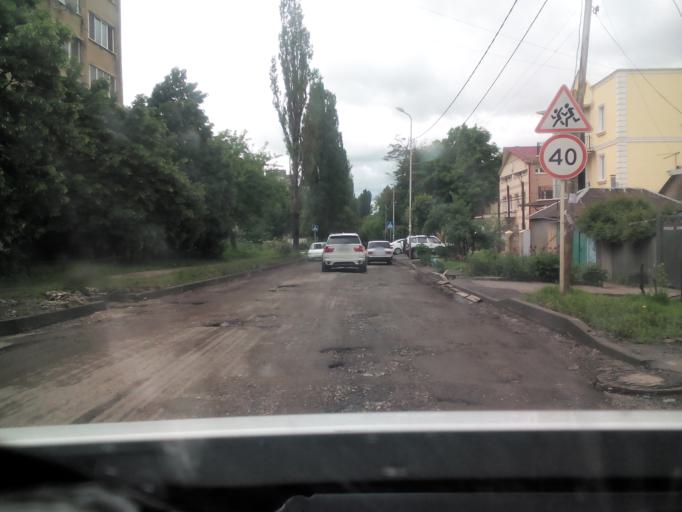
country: RU
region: Stavropol'skiy
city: Pyatigorsk
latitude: 44.0517
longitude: 43.0575
